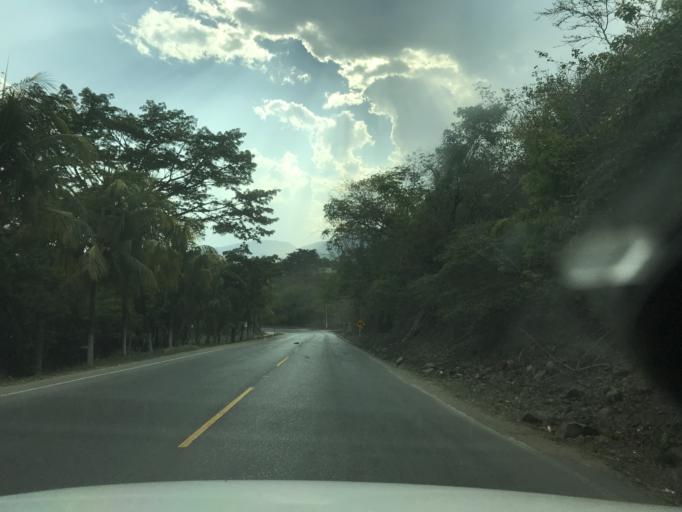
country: GT
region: Zacapa
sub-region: Municipio de Zacapa
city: Gualan
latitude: 15.1818
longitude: -89.3005
